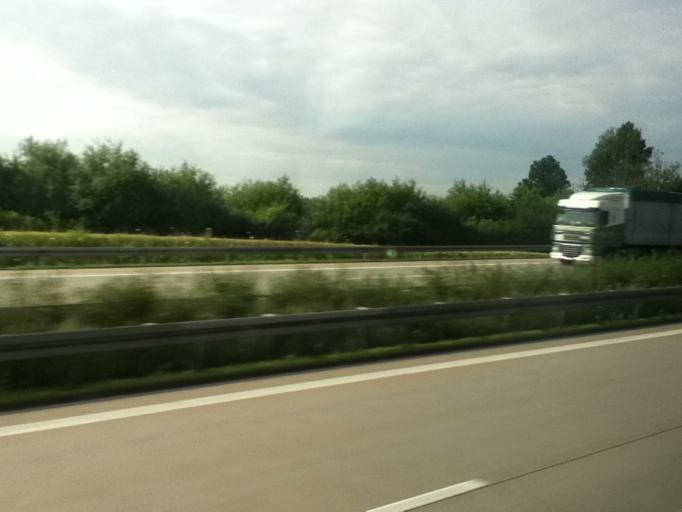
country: DE
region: Saxony
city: Hilbersdorf
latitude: 50.9003
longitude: 12.9599
